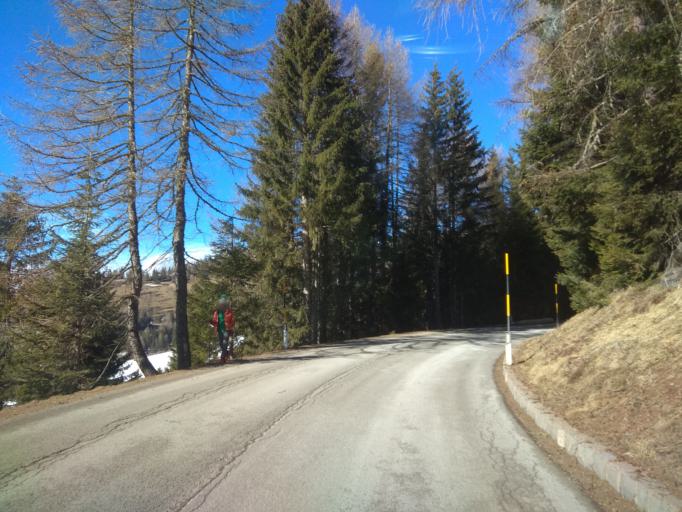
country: IT
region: Trentino-Alto Adige
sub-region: Bolzano
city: Nova Levante
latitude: 46.4272
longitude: 11.5976
